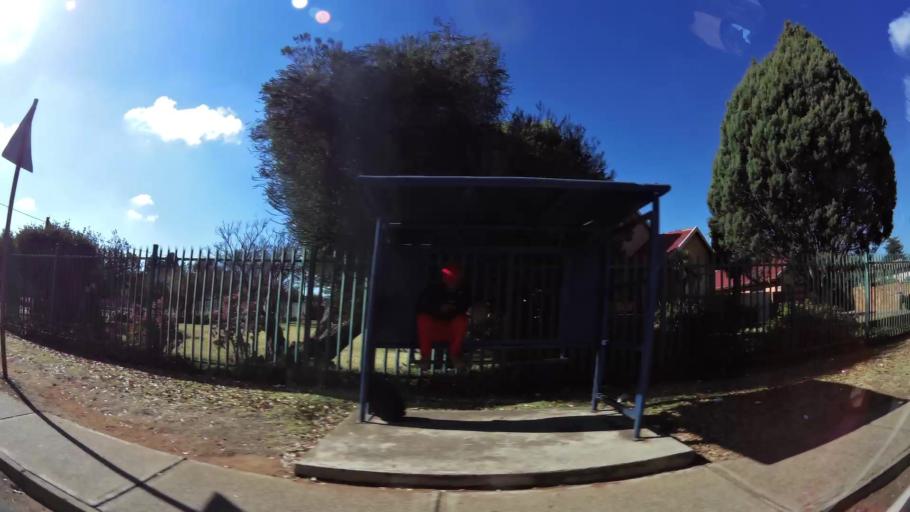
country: ZA
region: Gauteng
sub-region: City of Johannesburg Metropolitan Municipality
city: Roodepoort
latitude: -26.1391
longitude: 27.8326
